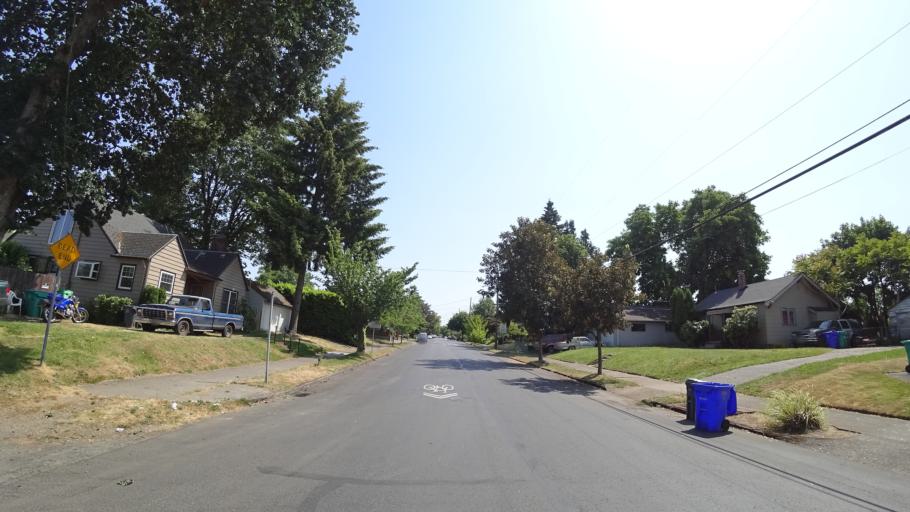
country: US
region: Oregon
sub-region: Multnomah County
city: Portland
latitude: 45.5815
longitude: -122.7027
